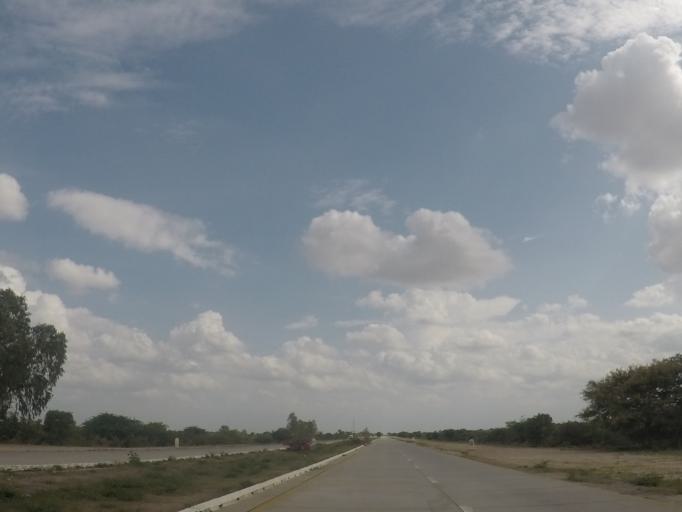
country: MM
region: Mandalay
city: Kyaukse
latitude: 21.4133
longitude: 95.9008
